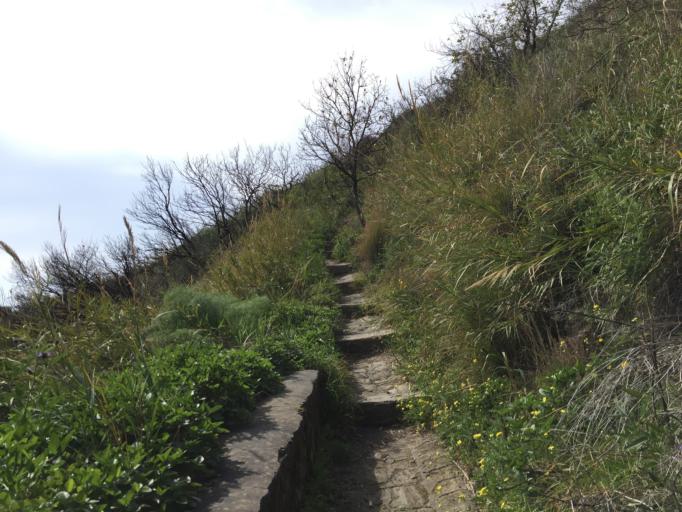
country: IT
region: Campania
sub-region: Provincia di Napoli
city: Bacoli
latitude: 40.7814
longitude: 14.0868
